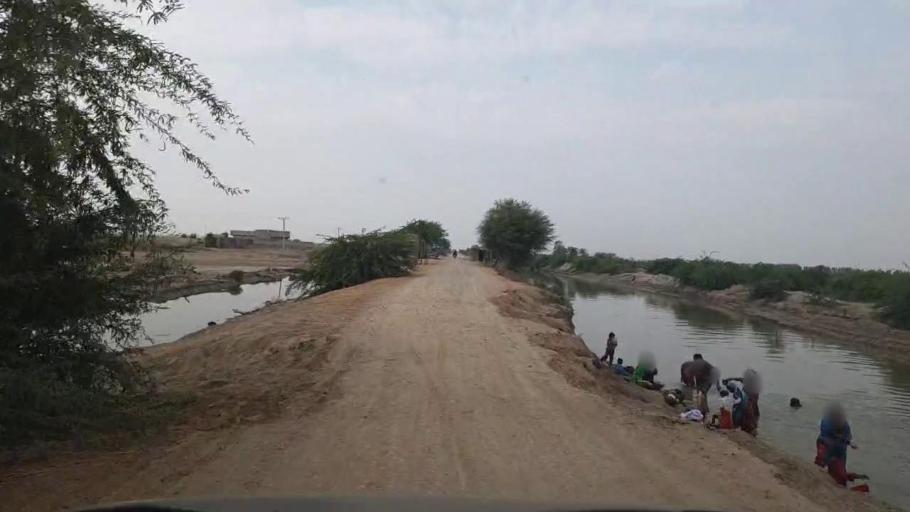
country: PK
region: Sindh
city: Kario
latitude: 24.6070
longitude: 68.5961
